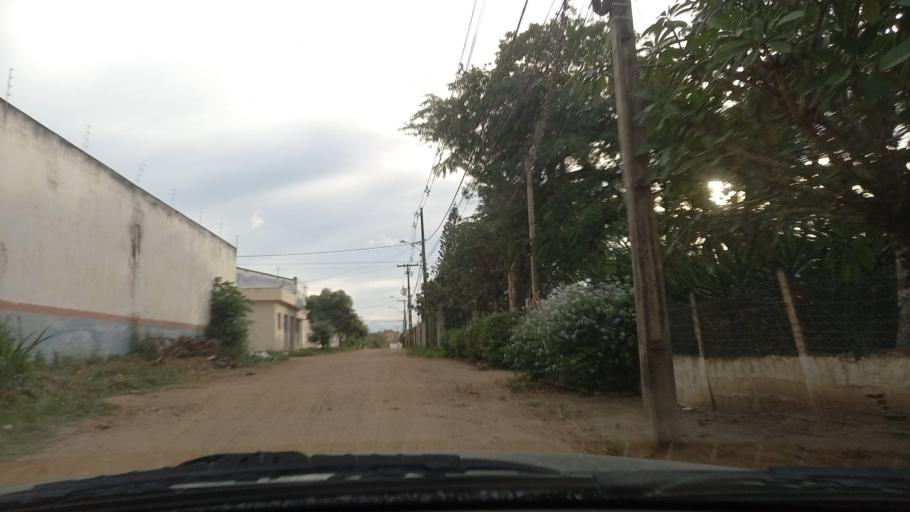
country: BR
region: Pernambuco
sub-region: Gravata
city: Gravata
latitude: -8.1937
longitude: -35.5706
